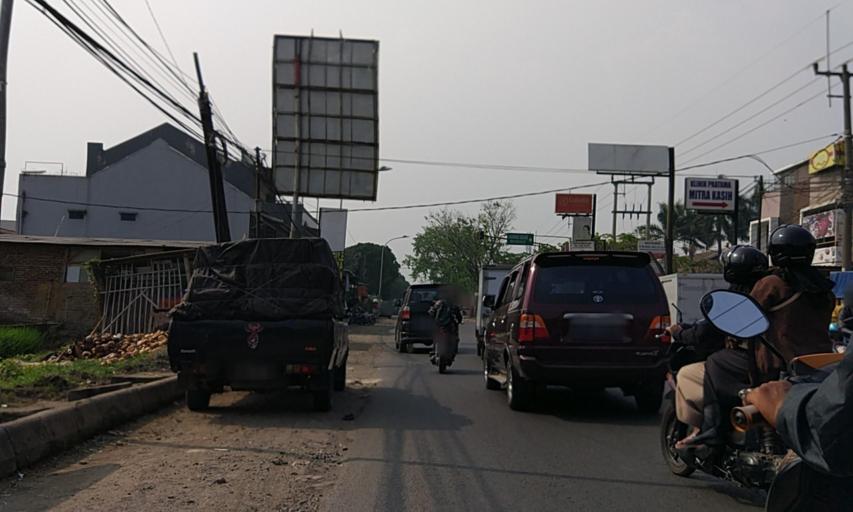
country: ID
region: West Java
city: Margahayukencana
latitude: -6.9970
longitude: 107.5543
